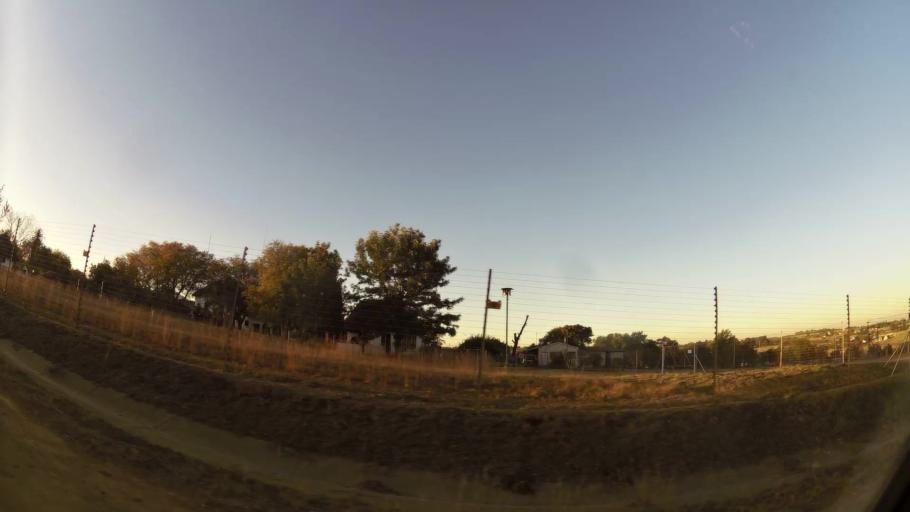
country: ZA
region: Gauteng
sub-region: City of Johannesburg Metropolitan Municipality
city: Diepsloot
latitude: -25.9409
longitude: 28.0534
